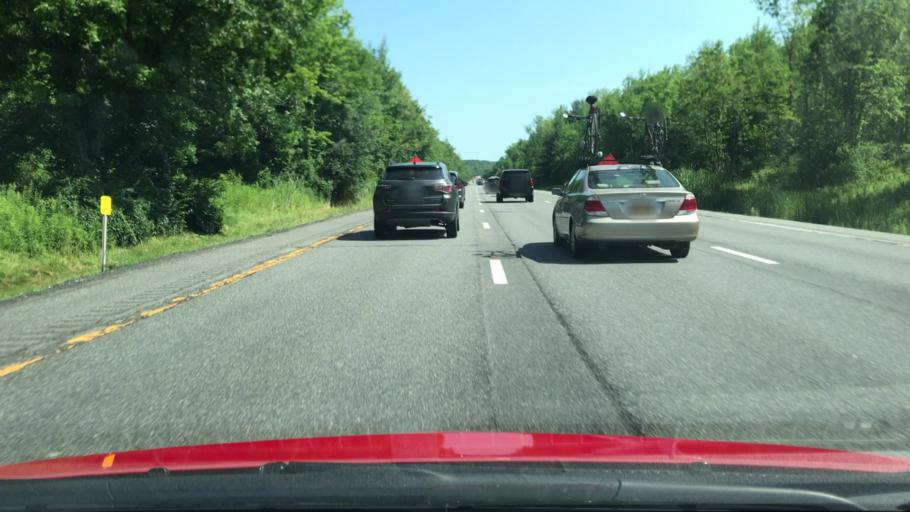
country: US
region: New York
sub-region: Saratoga County
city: Saratoga Springs
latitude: 43.0328
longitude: -73.7805
